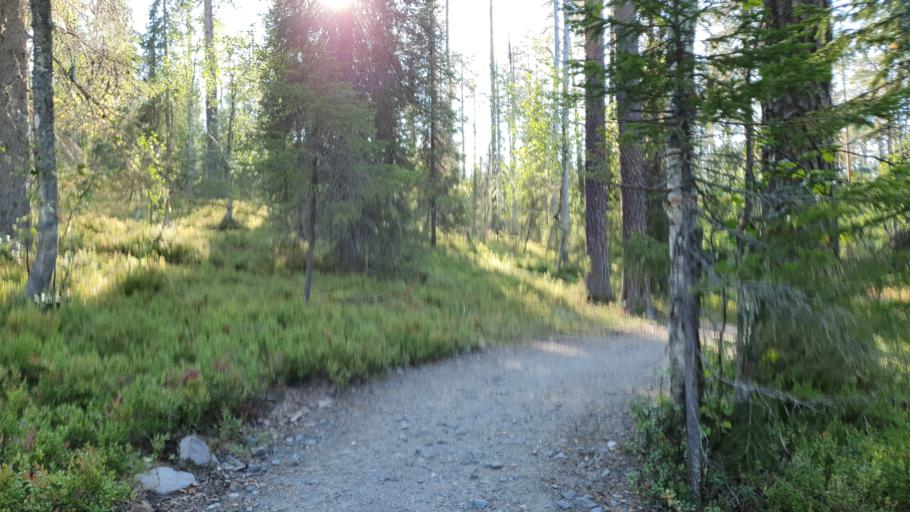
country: FI
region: Lapland
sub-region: Tunturi-Lappi
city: Kolari
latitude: 67.5972
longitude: 24.2228
